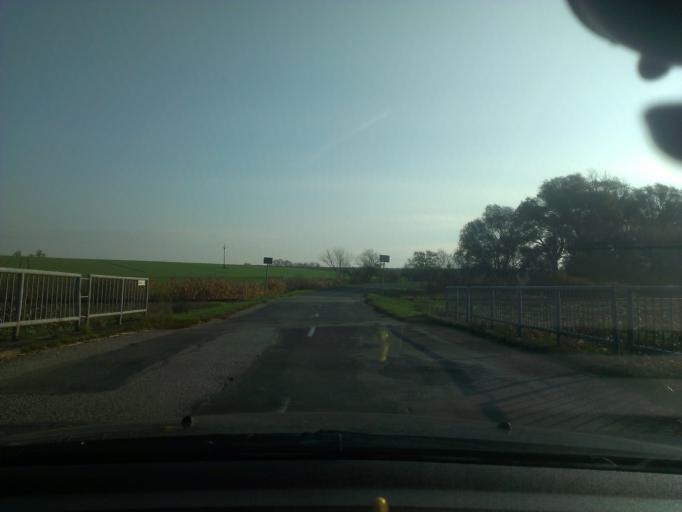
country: SK
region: Trnavsky
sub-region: Okres Trnava
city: Piestany
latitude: 48.5173
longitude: 17.9768
